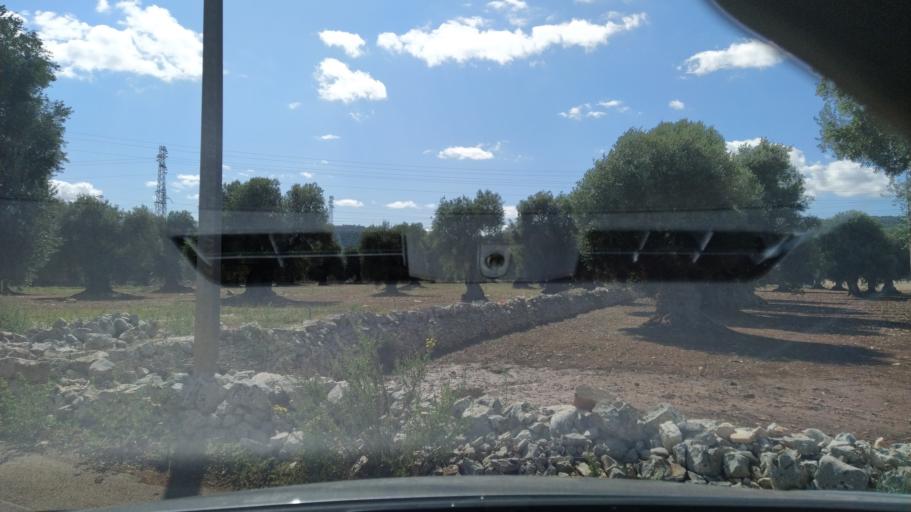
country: IT
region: Apulia
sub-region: Provincia di Brindisi
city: Fasano
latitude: 40.8262
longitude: 17.3629
